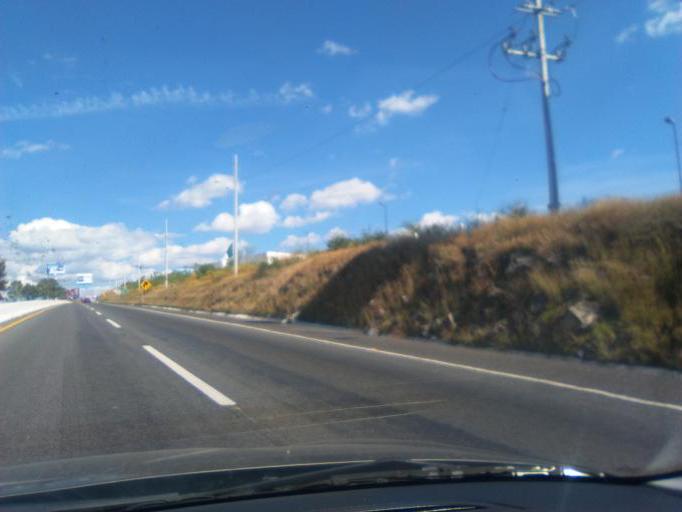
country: MX
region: Guanajuato
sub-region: Silao de la Victoria
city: Aguas Buenas
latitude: 20.9574
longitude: -101.3644
